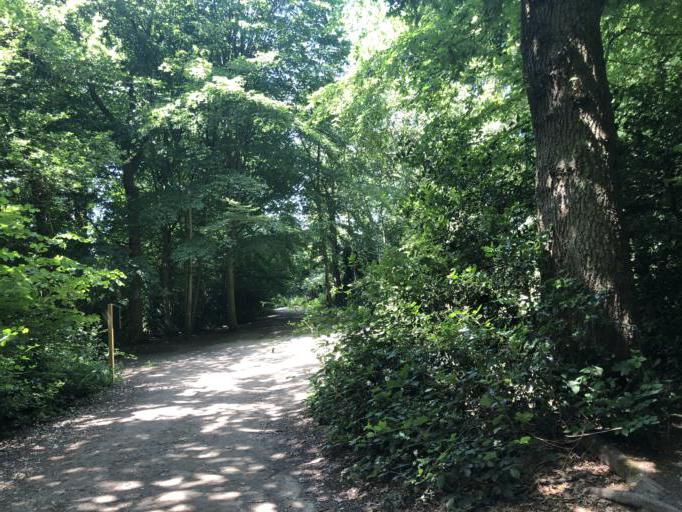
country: GB
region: England
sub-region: Greater London
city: Wandsworth
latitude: 51.4387
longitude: -0.2376
